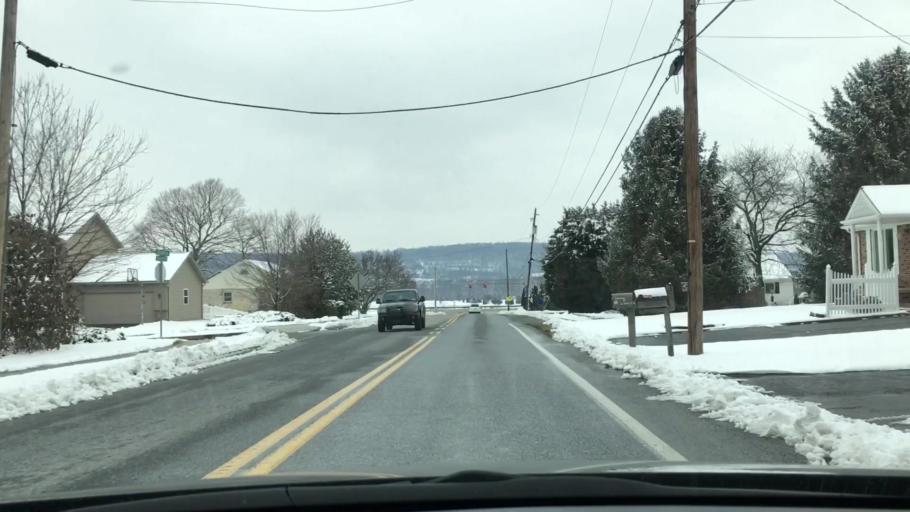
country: US
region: Pennsylvania
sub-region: York County
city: Emigsville
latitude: 40.0095
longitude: -76.7053
